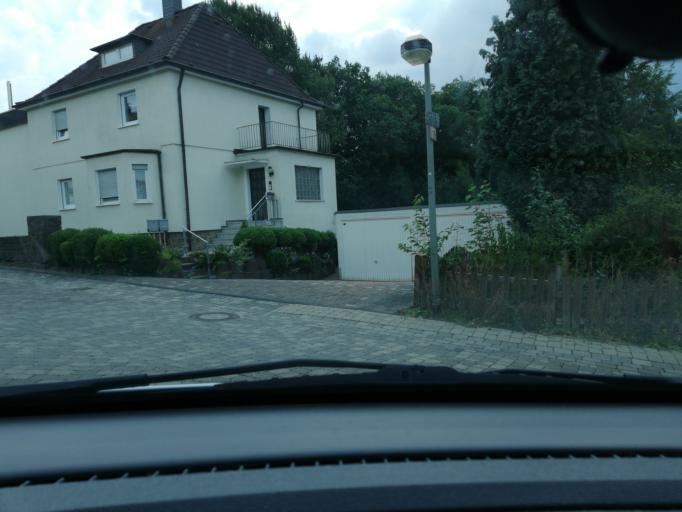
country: DE
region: North Rhine-Westphalia
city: Wetter (Ruhr)
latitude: 51.3747
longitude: 7.3653
